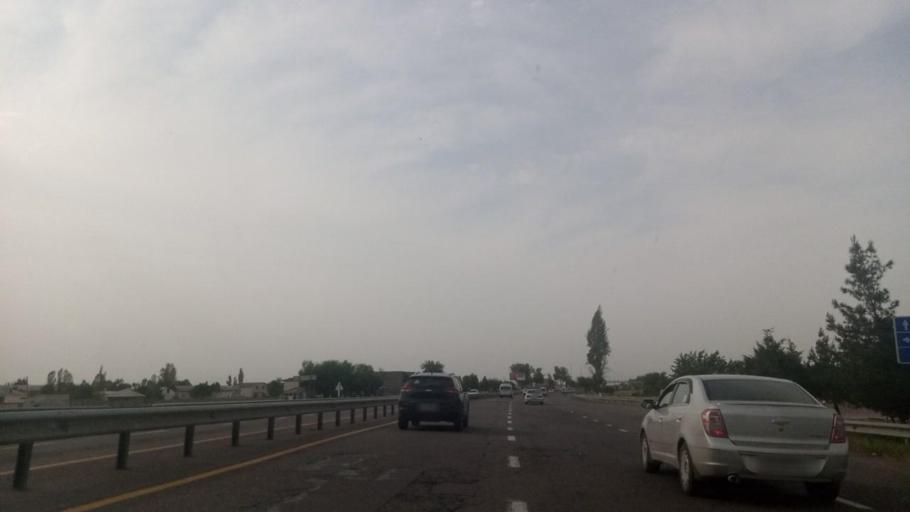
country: UZ
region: Toshkent
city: Tuytepa
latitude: 41.1251
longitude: 69.4387
